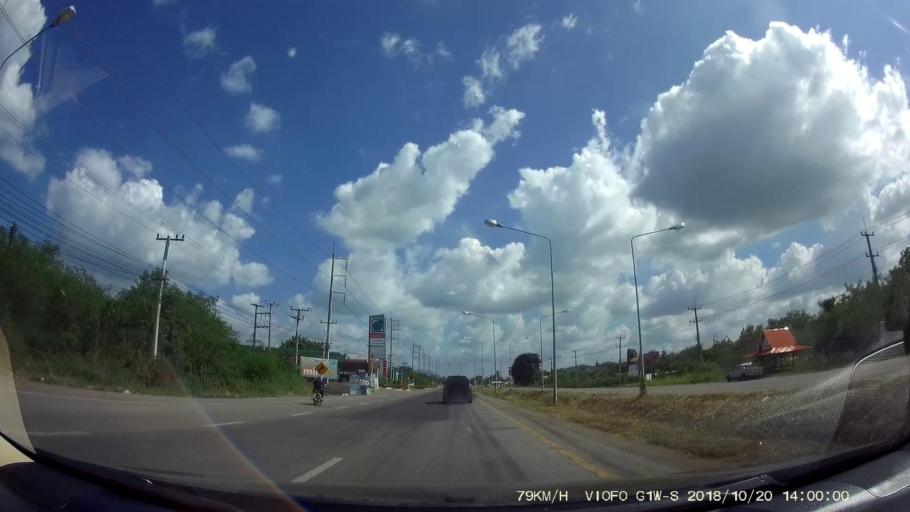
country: TH
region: Khon Kaen
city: Chum Phae
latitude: 16.5193
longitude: 102.1165
